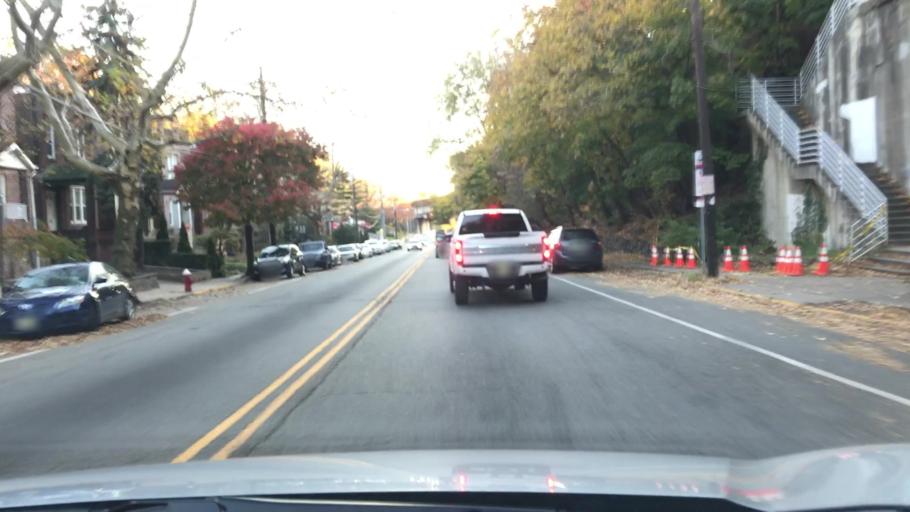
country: US
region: New Jersey
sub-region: Hudson County
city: Weehawken
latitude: 40.7705
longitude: -74.0208
